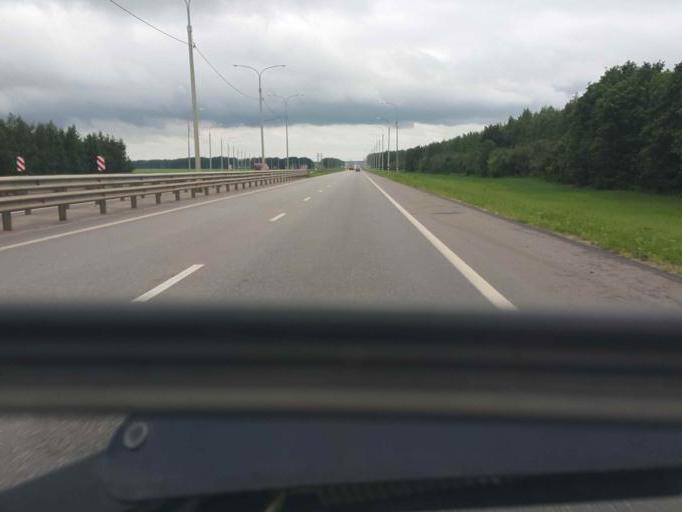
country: RU
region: Tambov
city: Zavoronezhskoye
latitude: 52.8448
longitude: 40.8253
